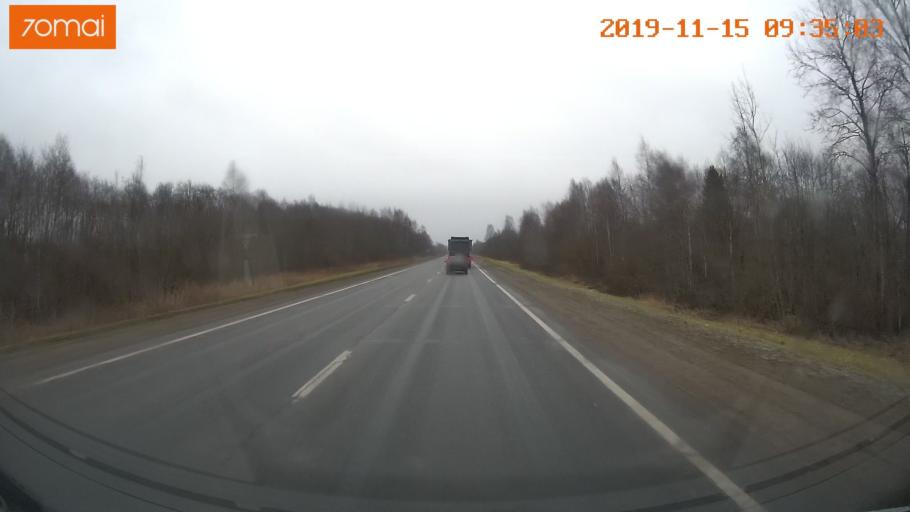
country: RU
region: Vologda
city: Sheksna
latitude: 59.2565
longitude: 38.3917
